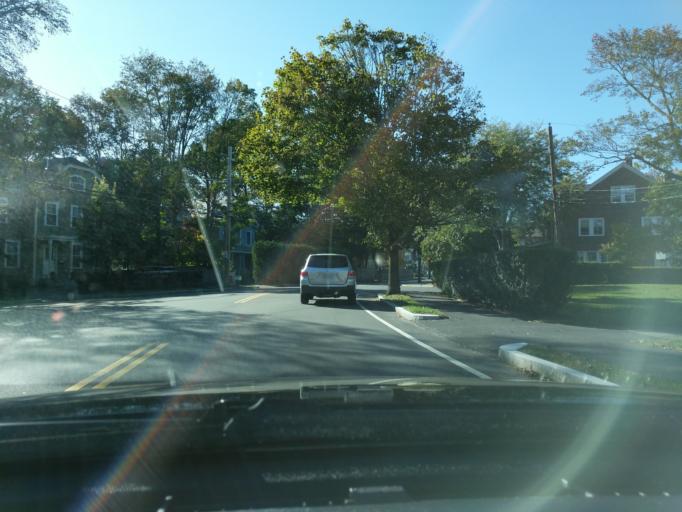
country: US
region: Massachusetts
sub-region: Middlesex County
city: Newton
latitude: 42.3445
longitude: -71.2394
